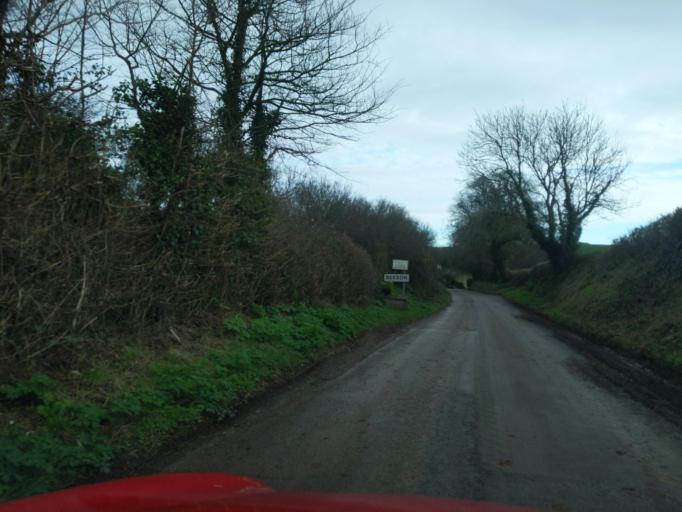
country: GB
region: England
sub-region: Devon
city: Salcombe
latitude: 50.2567
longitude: -3.6720
